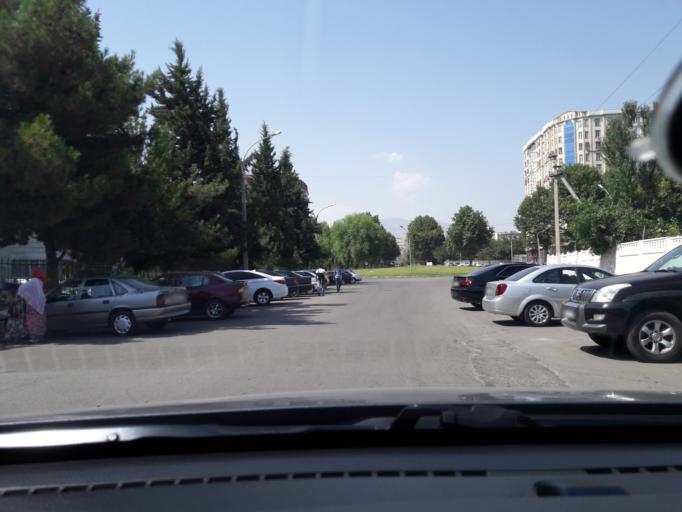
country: TJ
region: Dushanbe
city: Dushanbe
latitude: 38.5764
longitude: 68.7490
